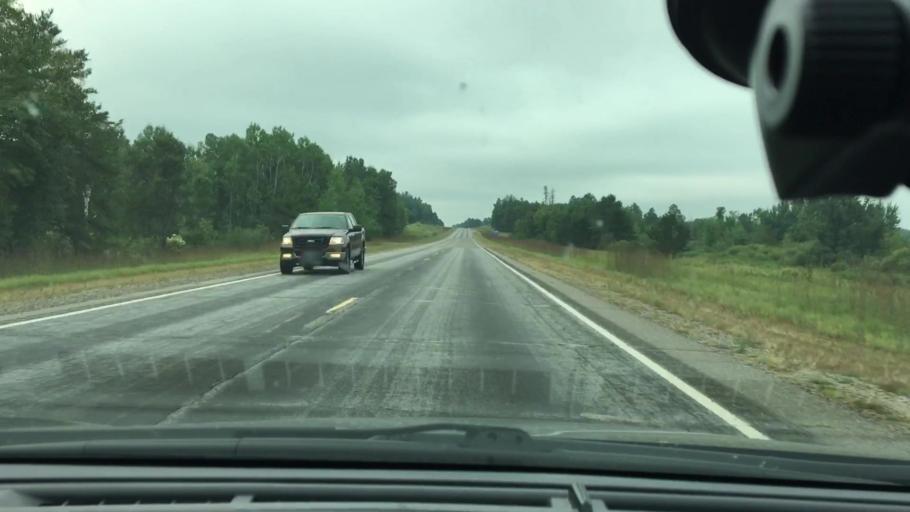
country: US
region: Minnesota
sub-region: Crow Wing County
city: Cross Lake
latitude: 46.6946
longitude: -93.9547
